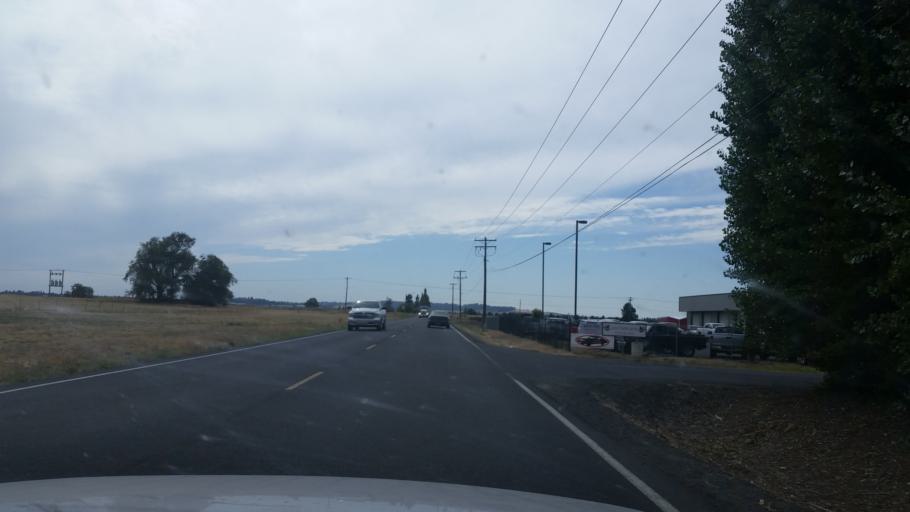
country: US
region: Washington
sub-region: Spokane County
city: Airway Heights
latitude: 47.6307
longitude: -117.5610
